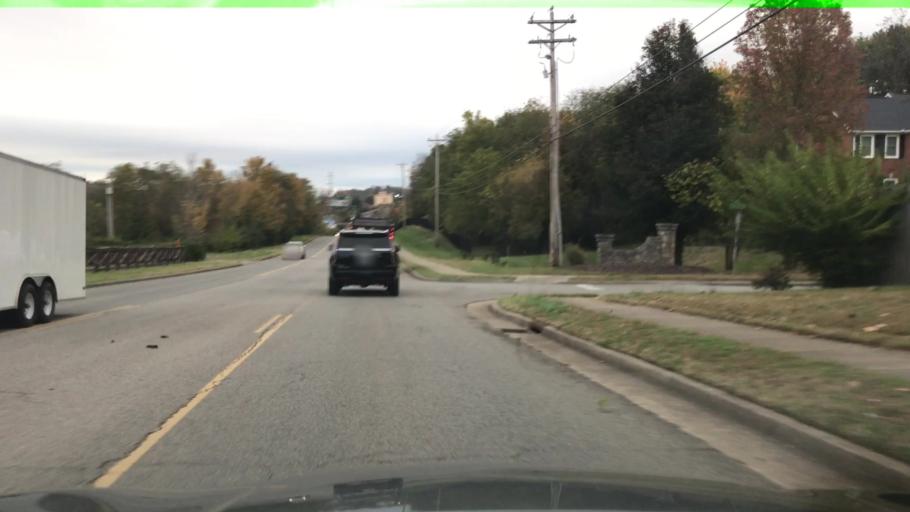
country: US
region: Tennessee
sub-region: Williamson County
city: Franklin
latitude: 35.9037
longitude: -86.8249
